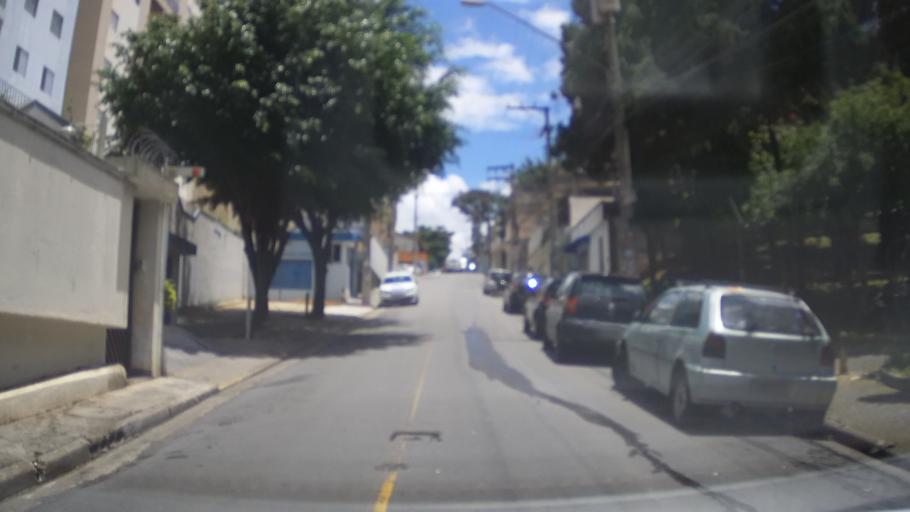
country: BR
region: Sao Paulo
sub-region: Guarulhos
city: Guarulhos
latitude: -23.4627
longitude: -46.5443
